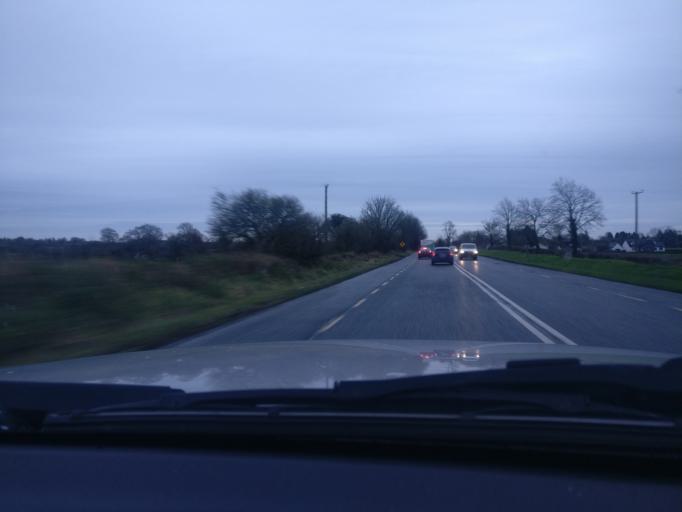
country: IE
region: Leinster
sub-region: An Mhi
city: Kells
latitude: 53.7092
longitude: -6.8037
